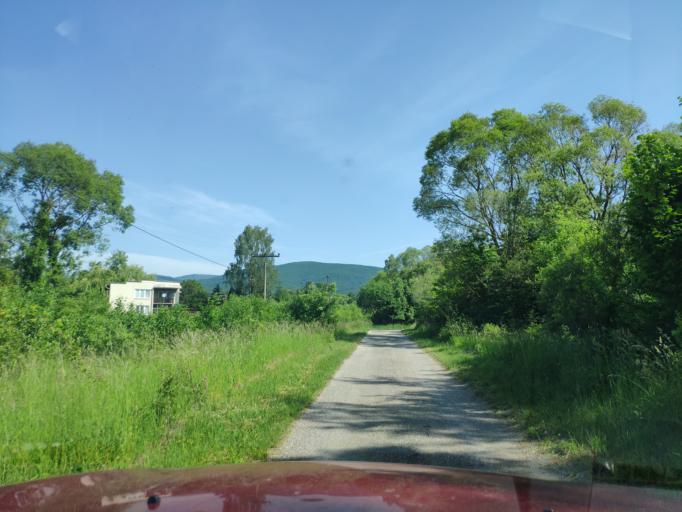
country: SK
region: Kosicky
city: Moldava nad Bodvou
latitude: 48.6895
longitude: 21.0123
